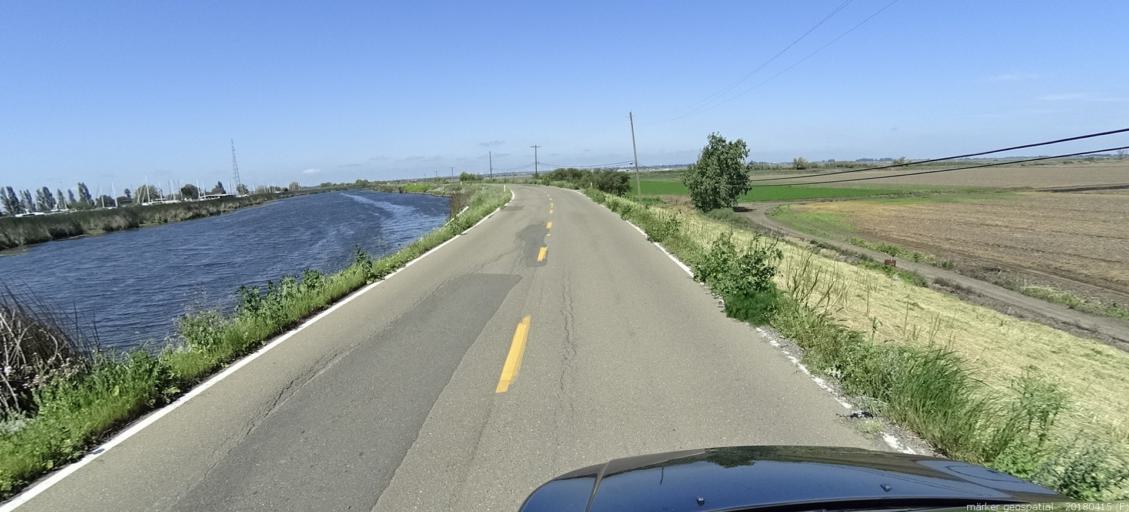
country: US
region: California
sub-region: Solano County
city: Rio Vista
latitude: 38.1170
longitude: -121.6207
